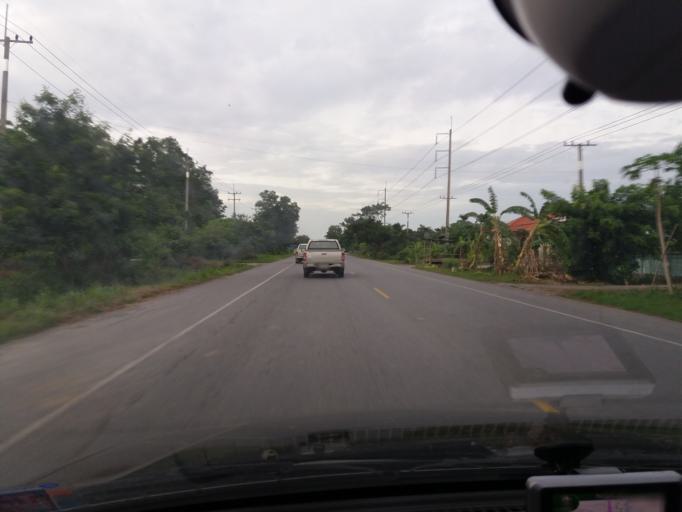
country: TH
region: Suphan Buri
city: U Thong
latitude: 14.5033
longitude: 99.9181
